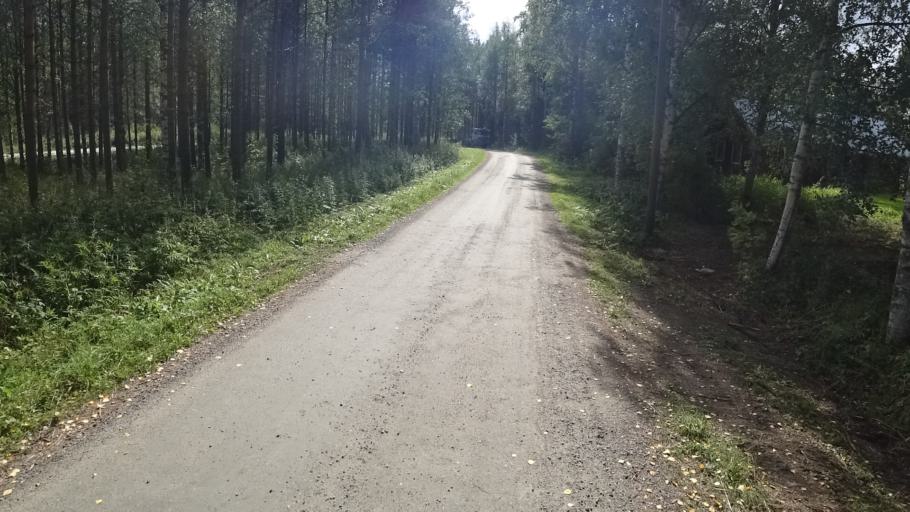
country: FI
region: North Karelia
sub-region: Joensuu
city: Ilomantsi
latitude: 62.6328
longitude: 31.2763
